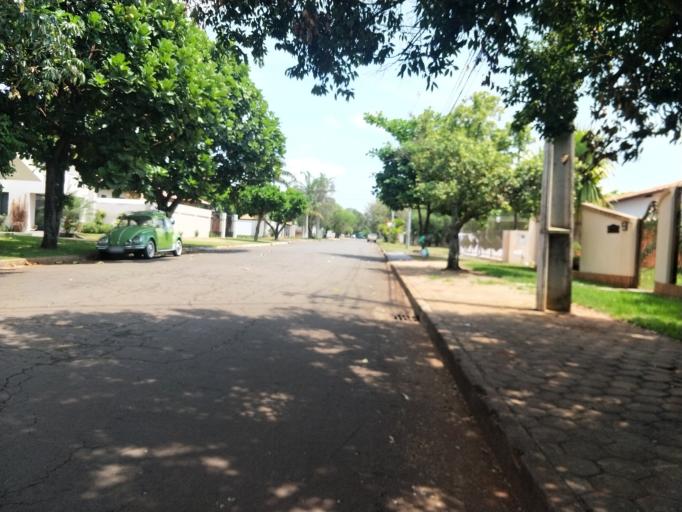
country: BR
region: Parana
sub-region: Marechal Candido Rondon
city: Marechal Candido Rondon
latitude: -24.5597
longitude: -54.0507
